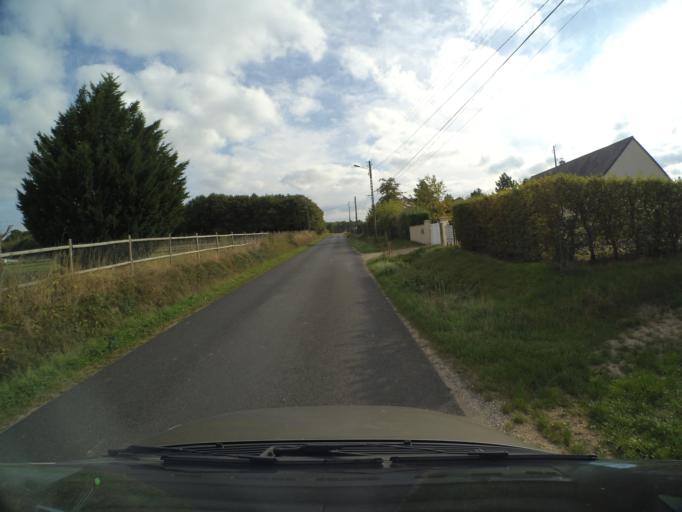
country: FR
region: Centre
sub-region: Departement d'Indre-et-Loire
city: Nazelles-Negron
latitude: 47.4704
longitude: 0.9540
